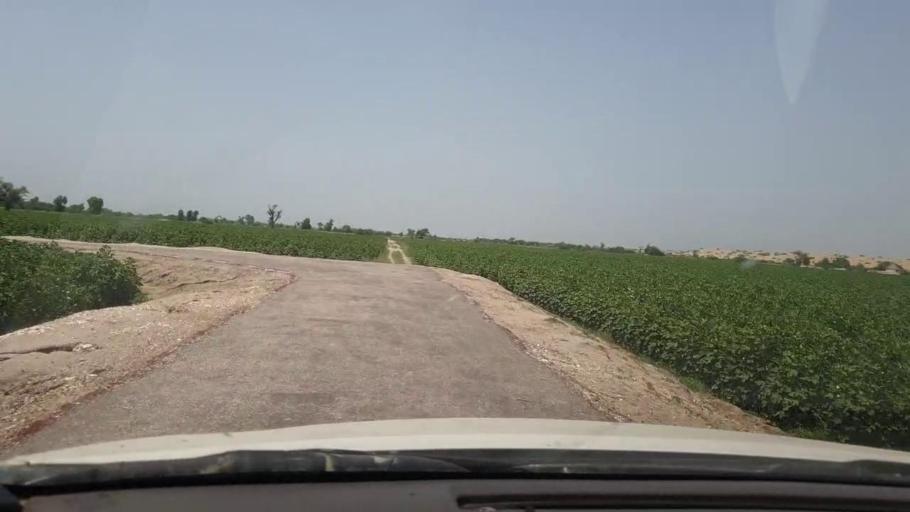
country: PK
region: Sindh
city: Rohri
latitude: 27.5221
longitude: 69.0625
